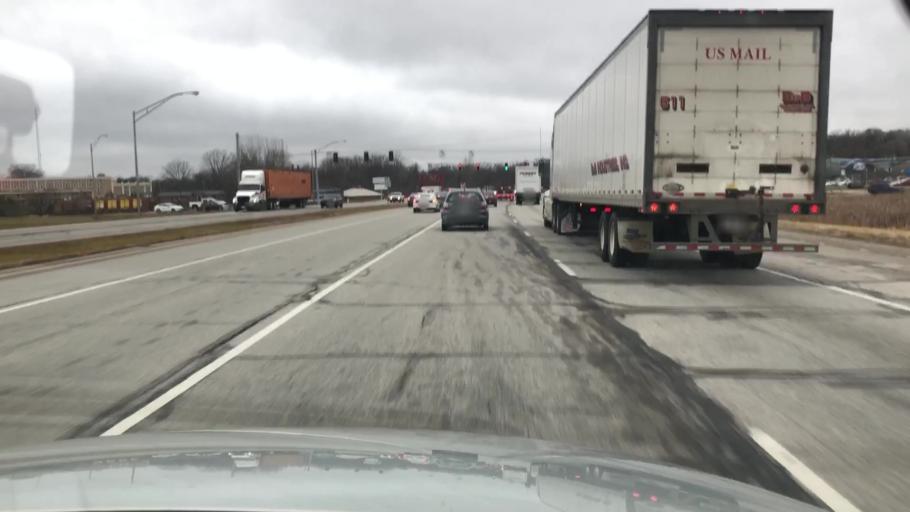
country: US
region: Indiana
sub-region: Kosciusko County
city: Winona Lake
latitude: 41.2381
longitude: -85.8142
